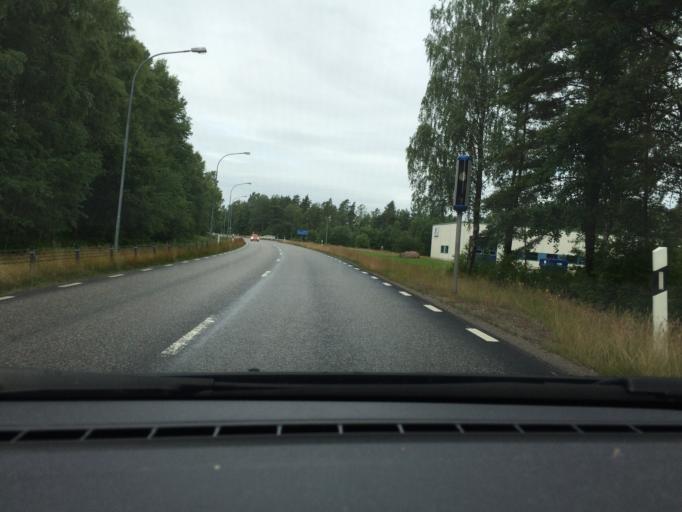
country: SE
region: Joenkoeping
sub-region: Varnamo Kommun
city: Forsheda
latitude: 57.1659
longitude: 13.8380
